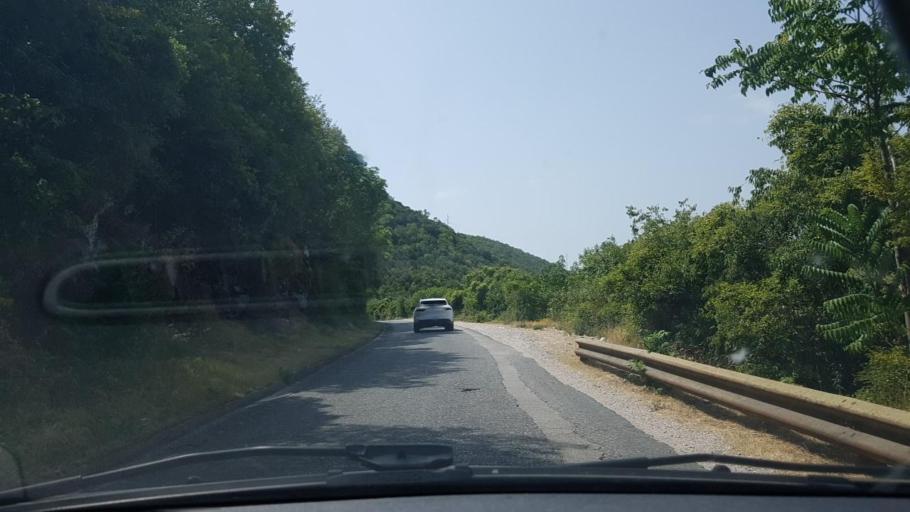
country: BA
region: Federation of Bosnia and Herzegovina
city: Tasovcici
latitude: 43.0284
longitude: 17.7483
